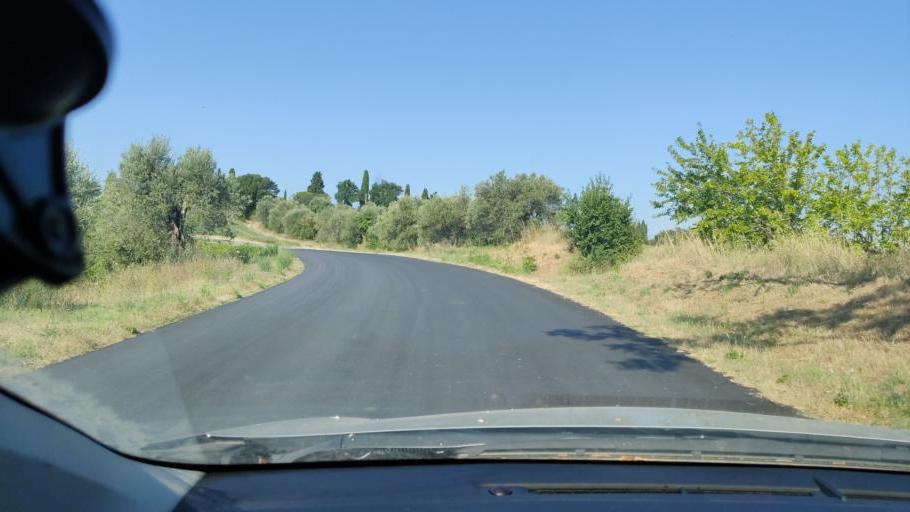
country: IT
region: Umbria
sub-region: Provincia di Terni
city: Fornole
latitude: 42.5251
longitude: 12.4358
